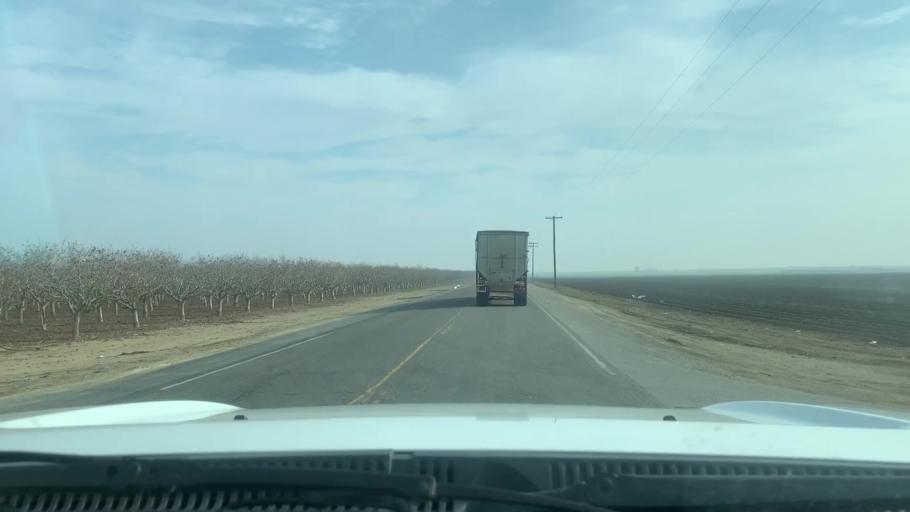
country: US
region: California
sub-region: Kern County
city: Shafter
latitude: 35.5001
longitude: -119.3678
